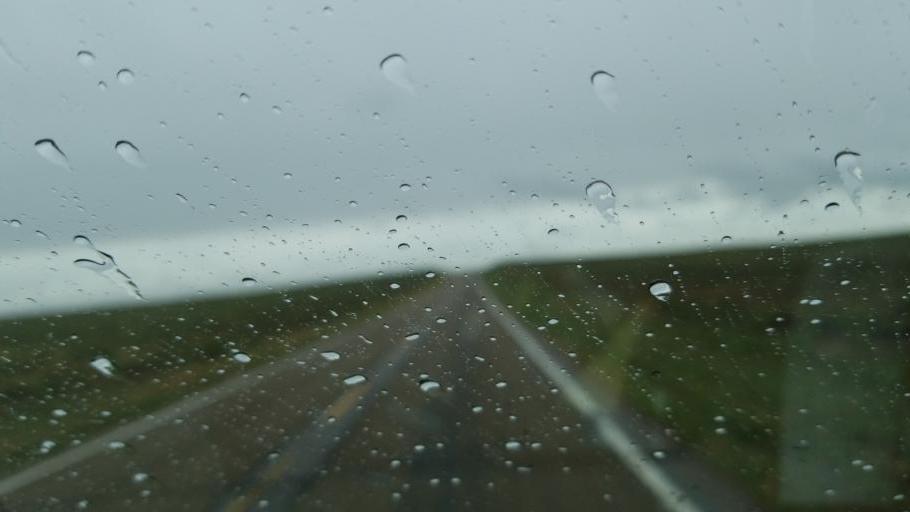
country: US
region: Colorado
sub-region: Lincoln County
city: Hugo
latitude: 38.8494
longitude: -103.2529
